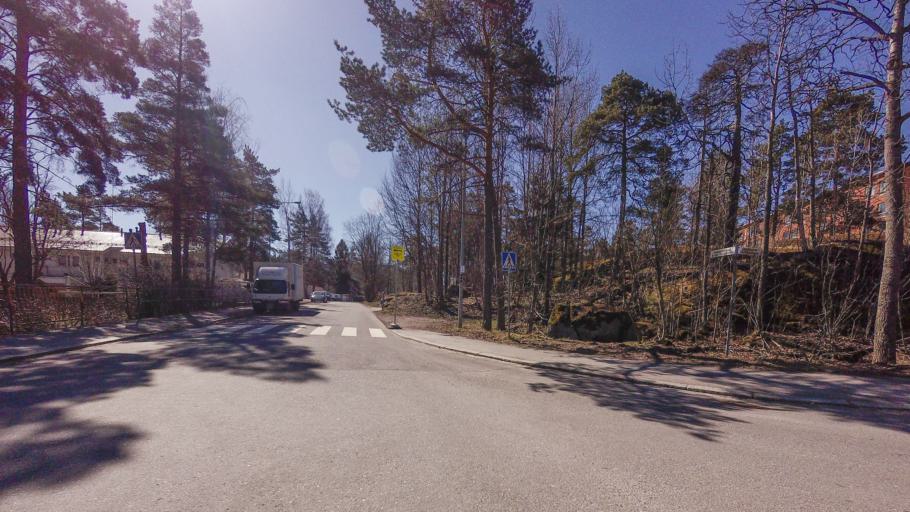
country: FI
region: Uusimaa
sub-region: Helsinki
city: Helsinki
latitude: 60.1677
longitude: 25.0464
